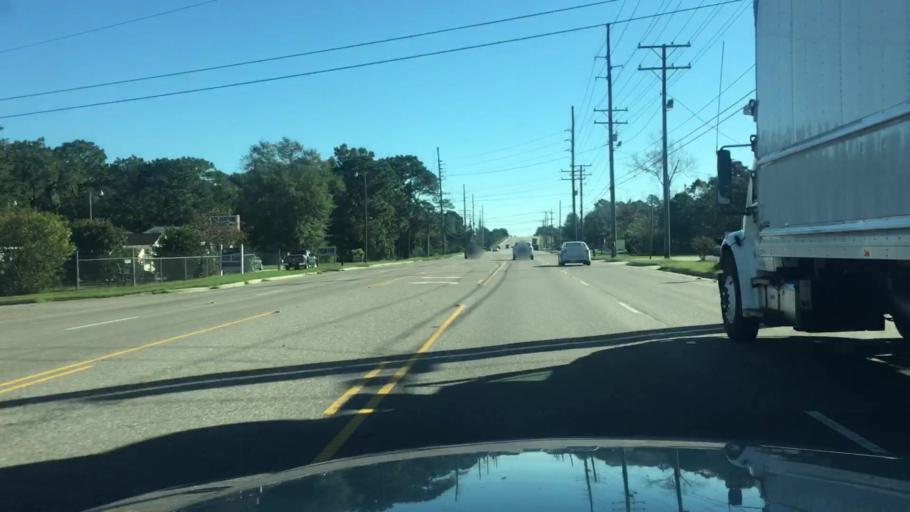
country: US
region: North Carolina
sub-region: Cumberland County
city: Hope Mills
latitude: 35.0153
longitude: -78.9307
